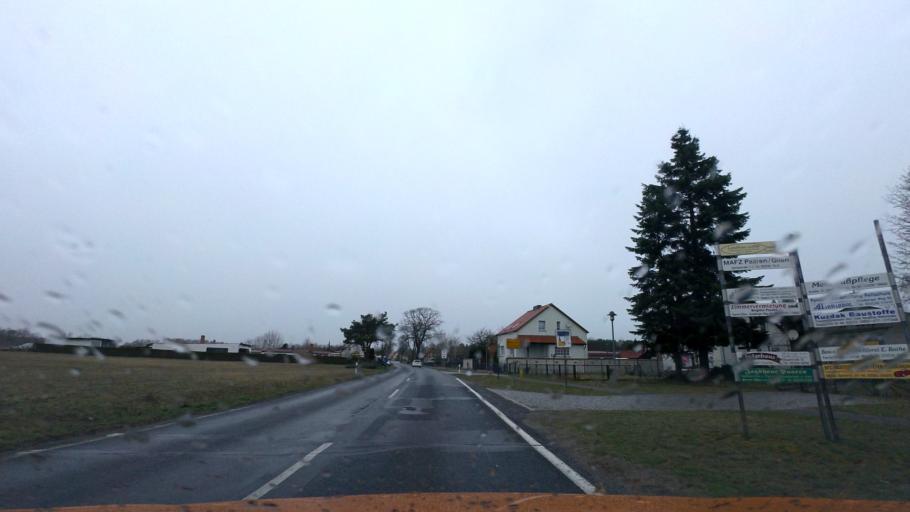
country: DE
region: Brandenburg
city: Brieselang
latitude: 52.6508
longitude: 12.9952
